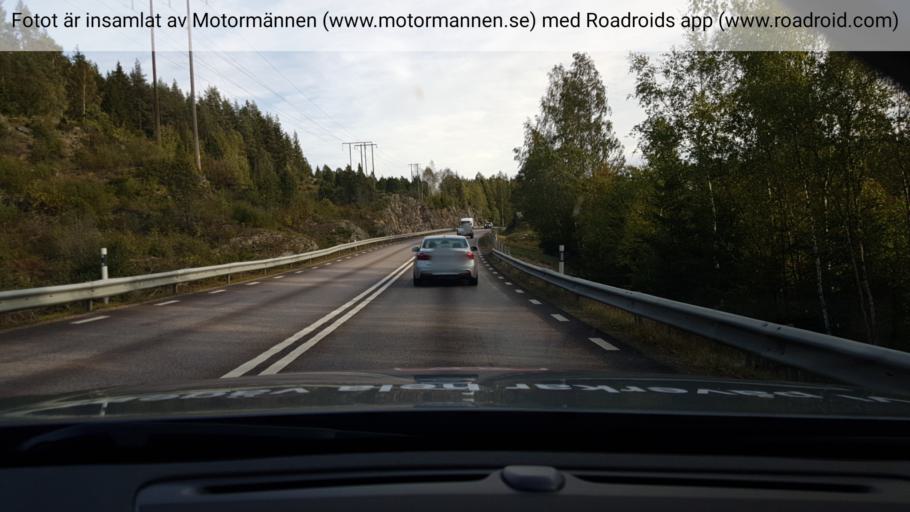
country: SE
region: Vaermland
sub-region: Arjangs Kommun
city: Toecksfors
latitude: 59.5034
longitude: 11.8699
